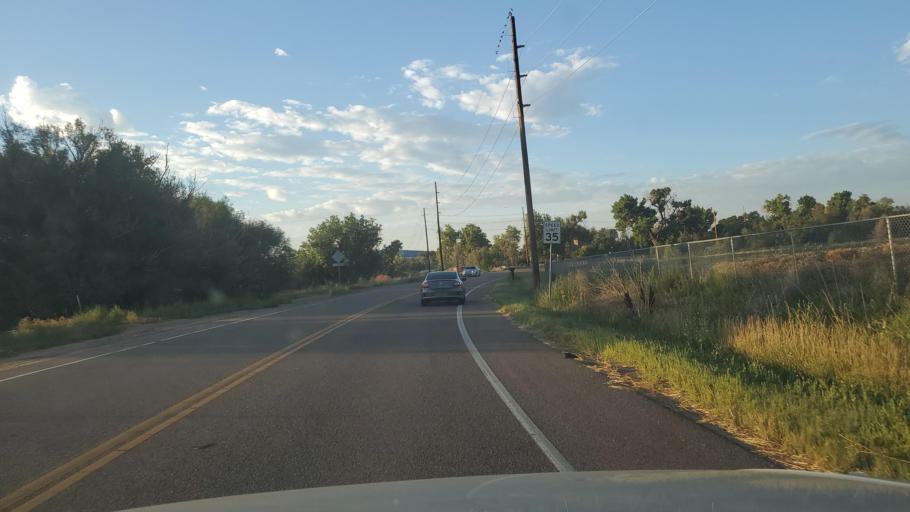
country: US
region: Colorado
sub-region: Adams County
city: Derby
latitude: 39.8700
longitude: -104.9110
